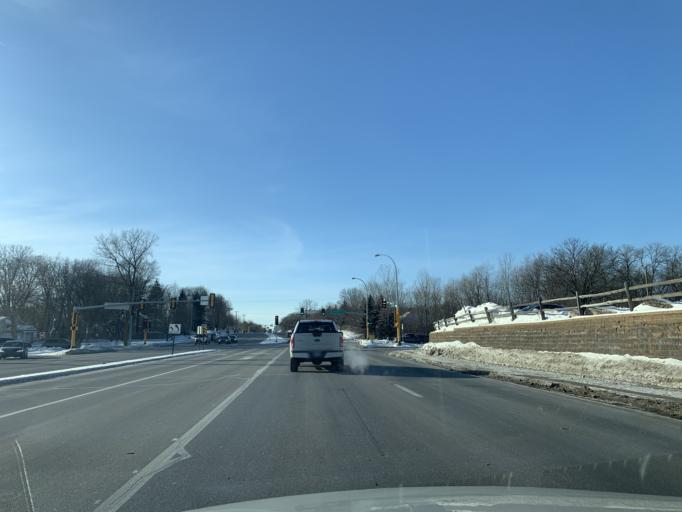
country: US
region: Minnesota
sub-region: Hennepin County
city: Plymouth
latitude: 45.0292
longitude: -93.4564
